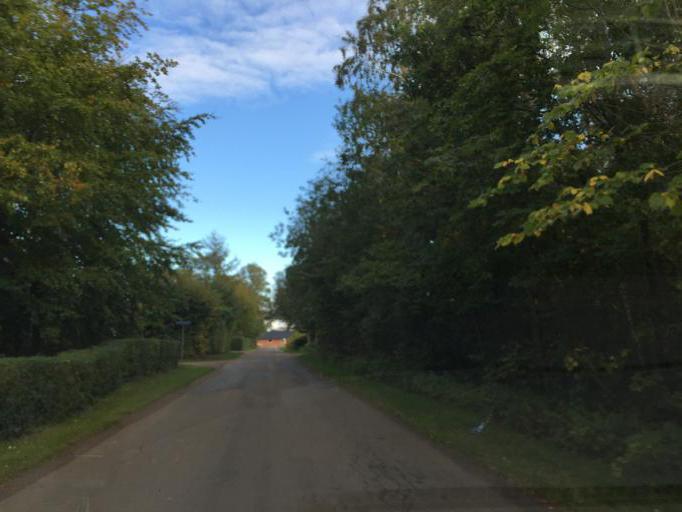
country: DK
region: Zealand
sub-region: Odsherred Kommune
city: Asnaes
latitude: 55.7964
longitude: 11.5020
